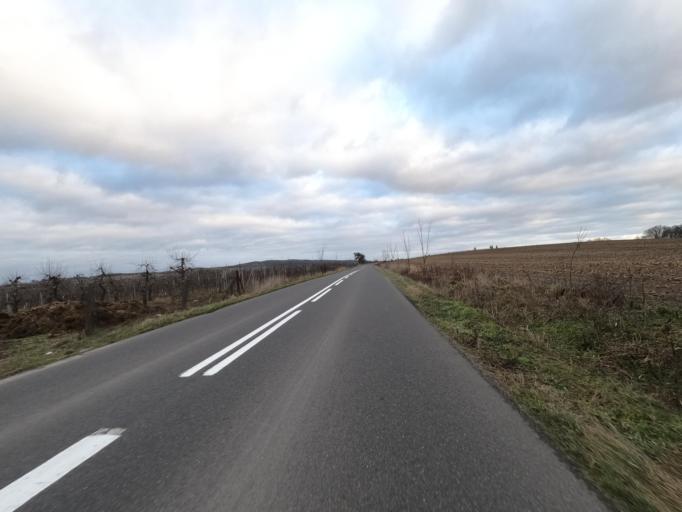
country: PL
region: Greater Poland Voivodeship
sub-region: Powiat pilski
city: Bialosliwie
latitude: 53.1104
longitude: 17.1598
